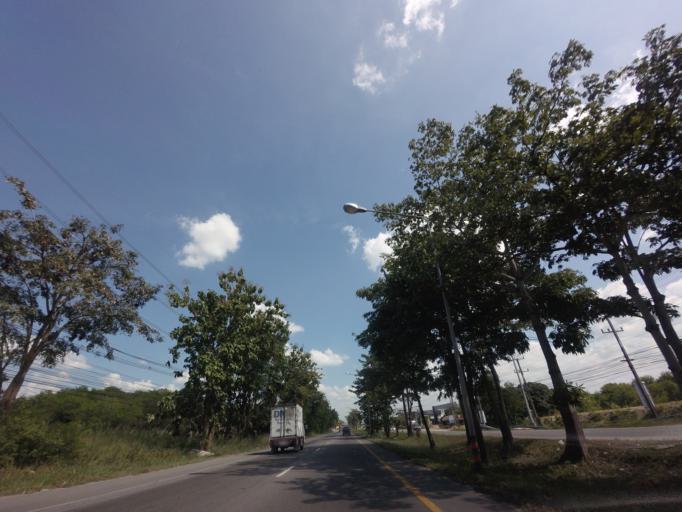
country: TH
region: Chon Buri
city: Ban Bueng
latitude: 13.3028
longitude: 101.1401
